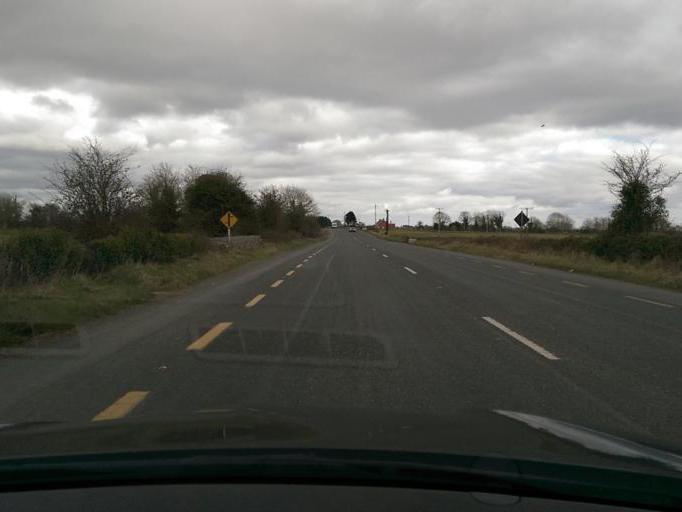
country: IE
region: Leinster
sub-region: An Iarmhi
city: Athlone
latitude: 53.3680
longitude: -8.0399
